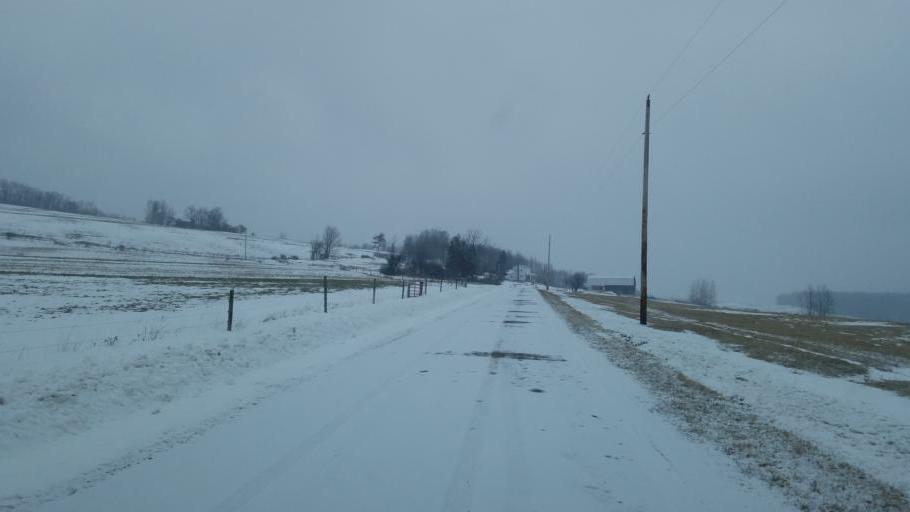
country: US
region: New York
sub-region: Steuben County
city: Canisteo
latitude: 42.1060
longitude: -77.5175
